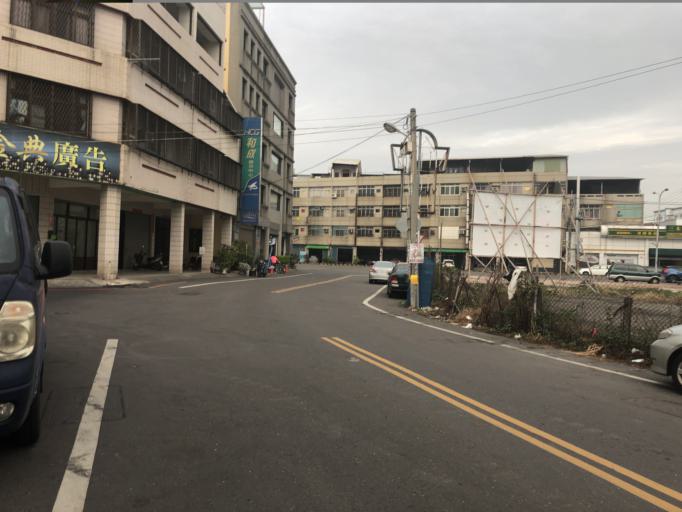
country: TW
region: Taiwan
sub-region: Changhua
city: Chang-hua
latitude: 23.9672
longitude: 120.5661
